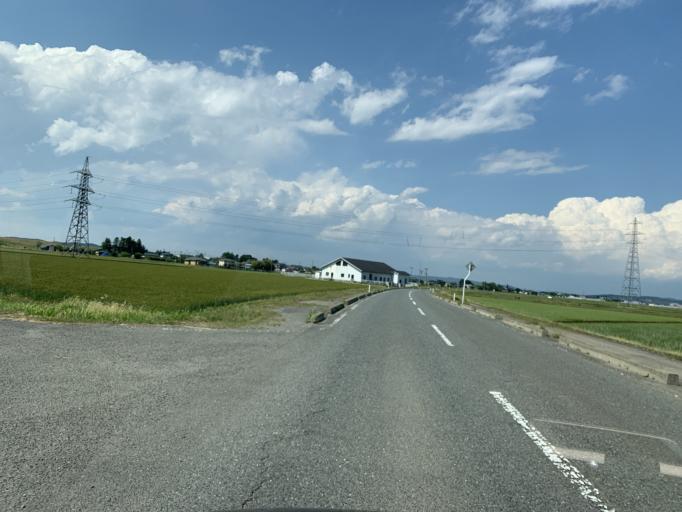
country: JP
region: Miyagi
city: Matsushima
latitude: 38.4506
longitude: 141.1119
